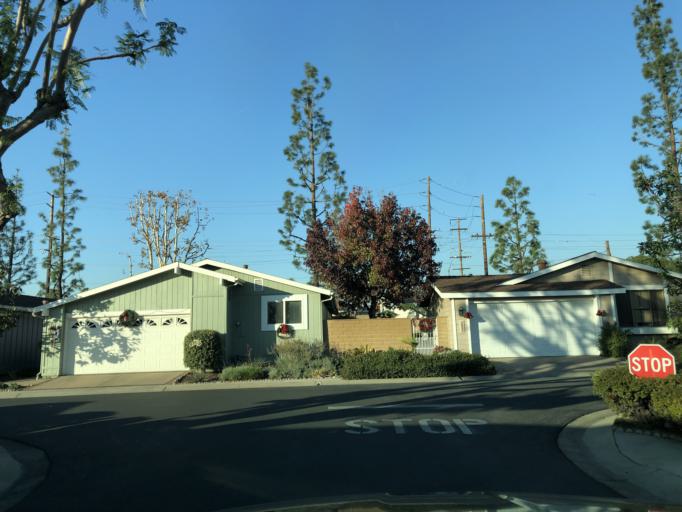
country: US
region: California
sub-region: Orange County
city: Orange
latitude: 33.7727
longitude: -117.8448
